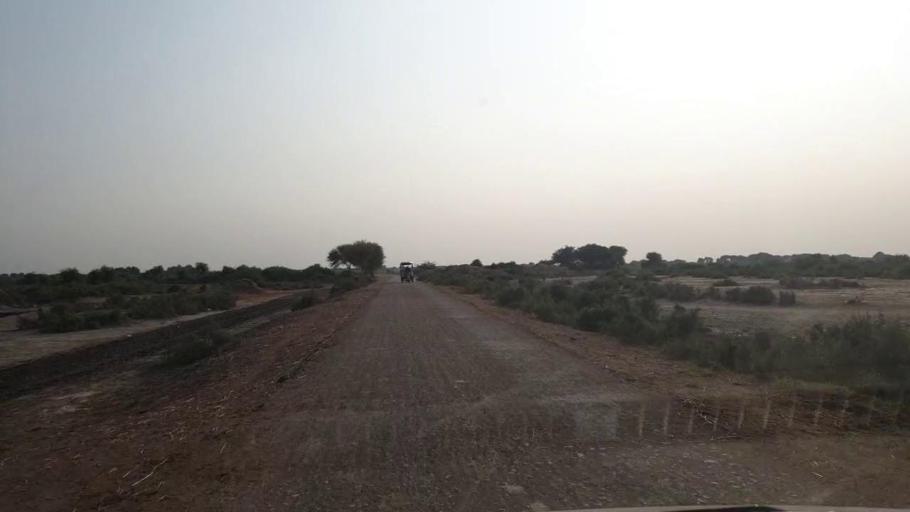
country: PK
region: Sindh
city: Rajo Khanani
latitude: 25.0108
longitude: 68.7865
